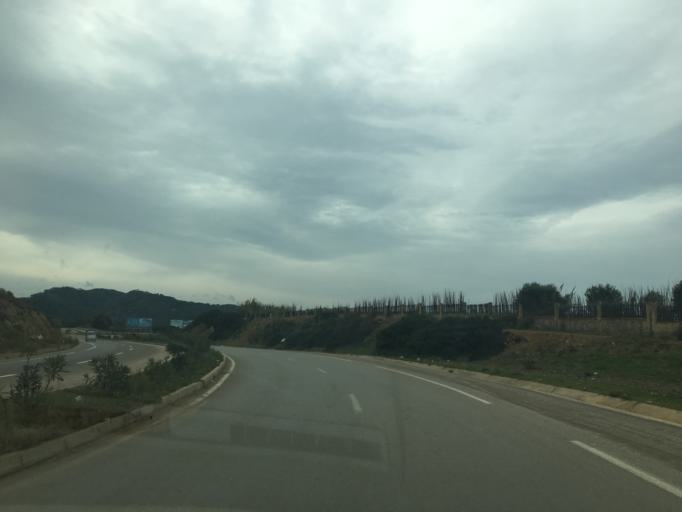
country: DZ
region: Tipaza
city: Tipasa
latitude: 36.6245
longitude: 2.2662
